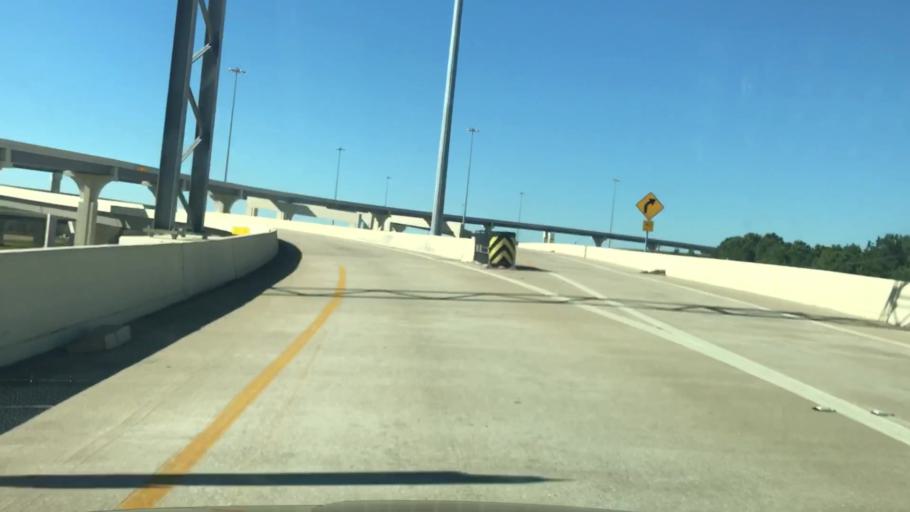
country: US
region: Texas
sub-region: Harris County
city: Cypress
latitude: 29.9979
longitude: -95.7658
